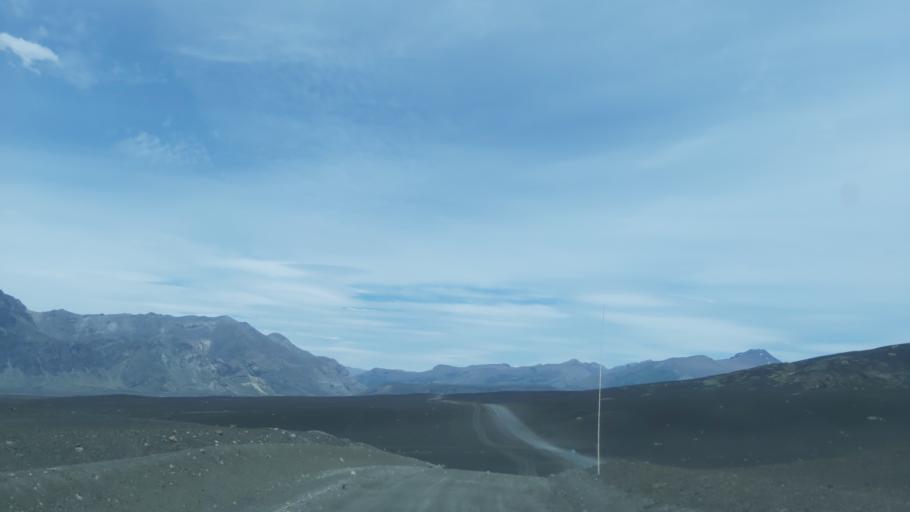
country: AR
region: Neuquen
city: Andacollo
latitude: -37.4220
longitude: -71.2877
